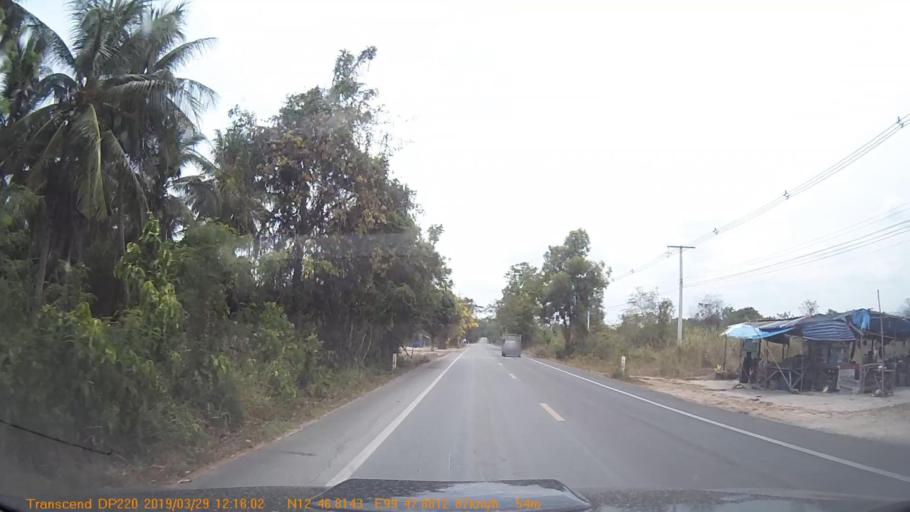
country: TH
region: Phetchaburi
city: Cha-am
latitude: 12.7797
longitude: 99.7980
